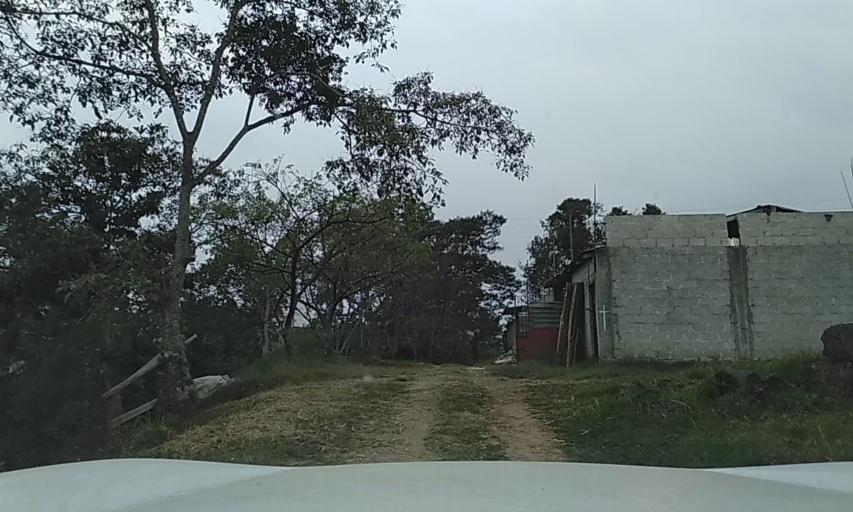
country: MX
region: Veracruz
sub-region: Jilotepec
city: El Pueblito (Garbanzal)
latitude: 19.5722
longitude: -96.8970
